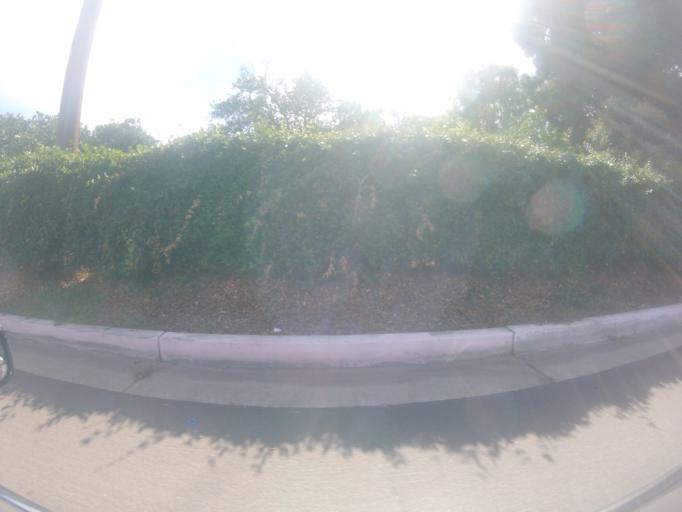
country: US
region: California
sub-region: San Bernardino County
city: Mentone
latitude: 34.0555
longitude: -117.1515
